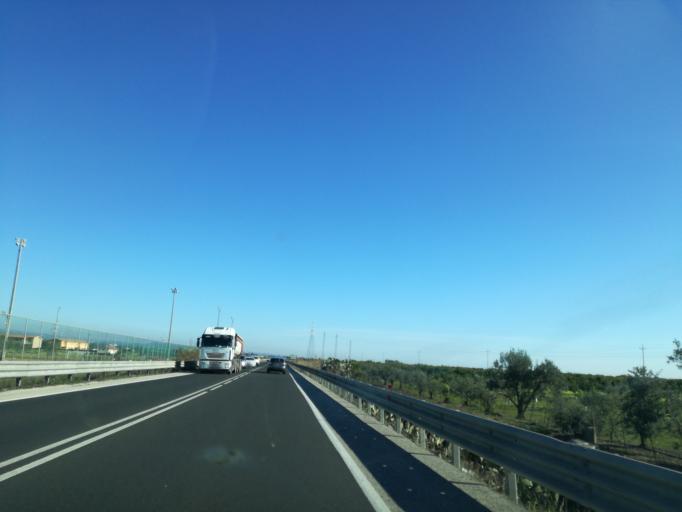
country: IT
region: Sicily
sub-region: Catania
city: Motta Sant'Anastasia
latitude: 37.4181
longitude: 14.9112
